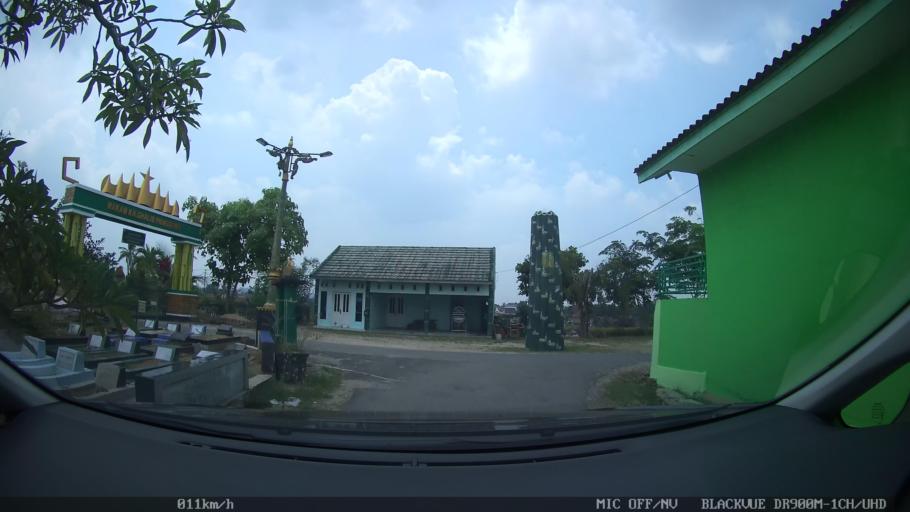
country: ID
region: Lampung
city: Pringsewu
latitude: -5.3477
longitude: 104.9702
